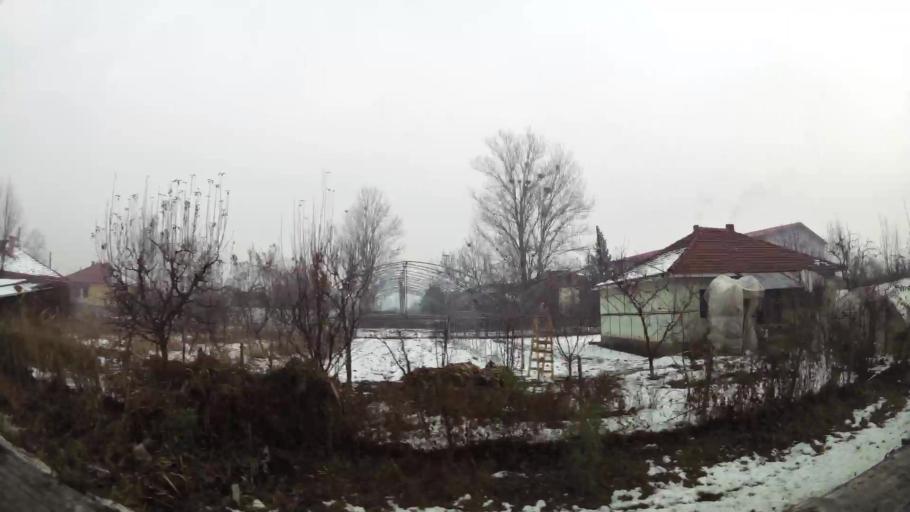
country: MK
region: Ilinden
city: Idrizovo
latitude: 41.9551
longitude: 21.5757
